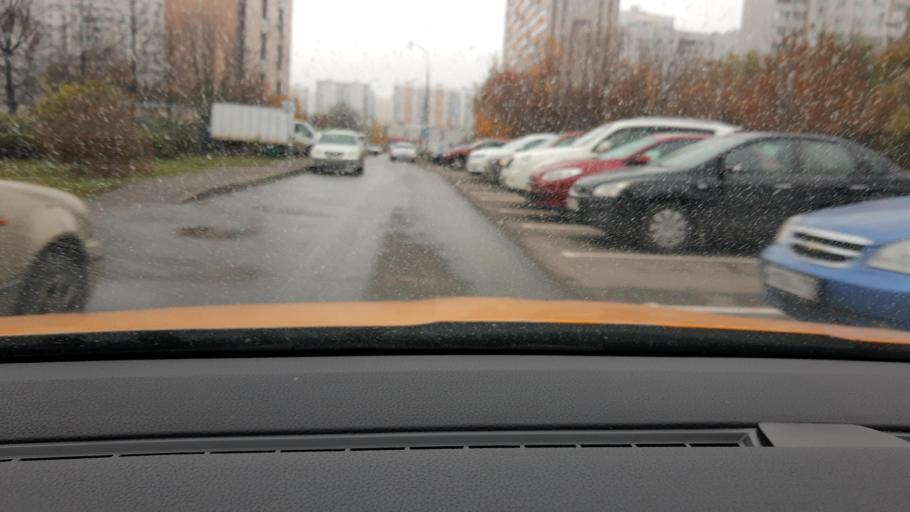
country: RU
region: Moscow
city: Novo-Peredelkino
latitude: 55.6419
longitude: 37.3523
